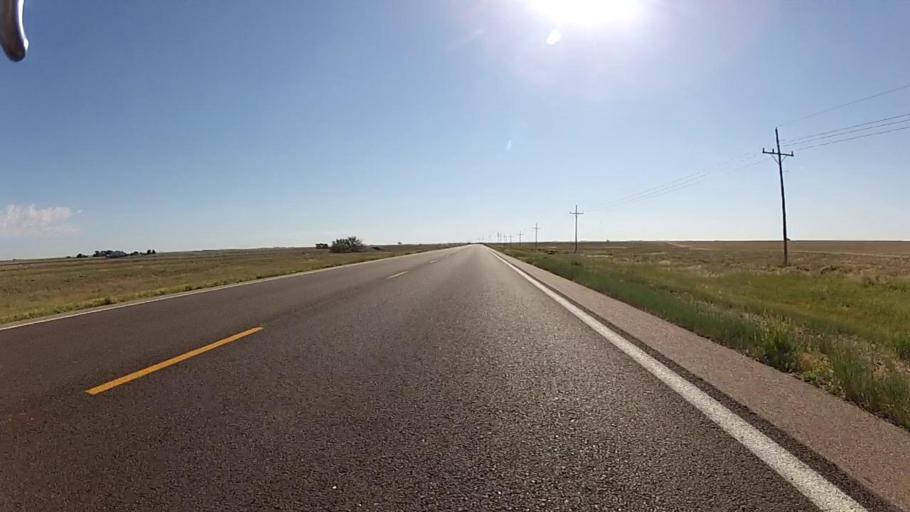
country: US
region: Kansas
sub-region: Haskell County
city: Sublette
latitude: 37.5552
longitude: -100.5848
